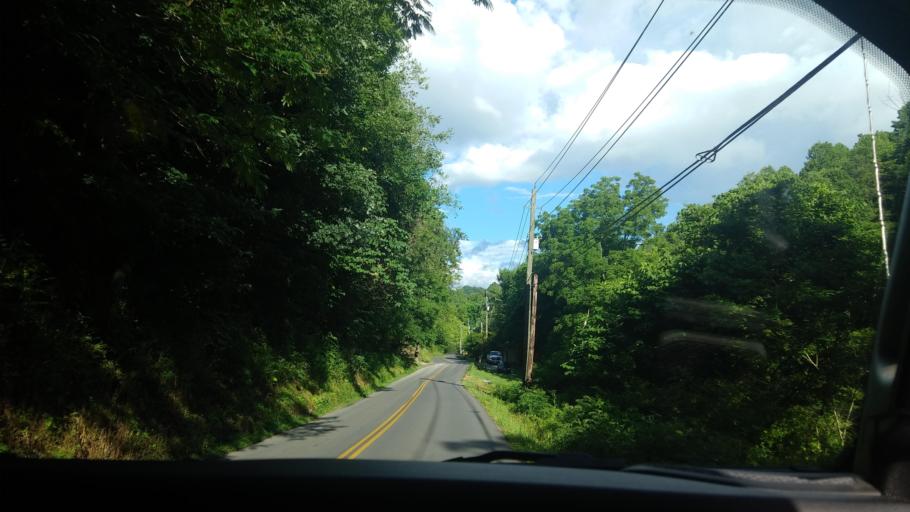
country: US
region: Tennessee
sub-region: Sevier County
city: Pigeon Forge
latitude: 35.7649
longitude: -83.5725
